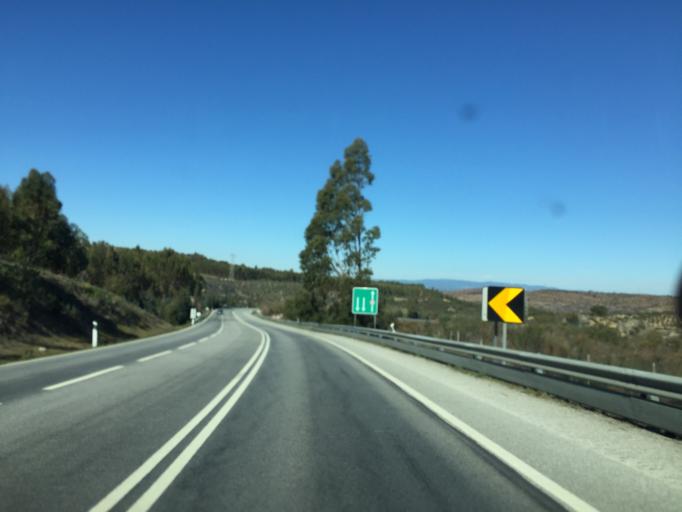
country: PT
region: Portalegre
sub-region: Nisa
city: Nisa
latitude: 39.5032
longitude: -7.7688
